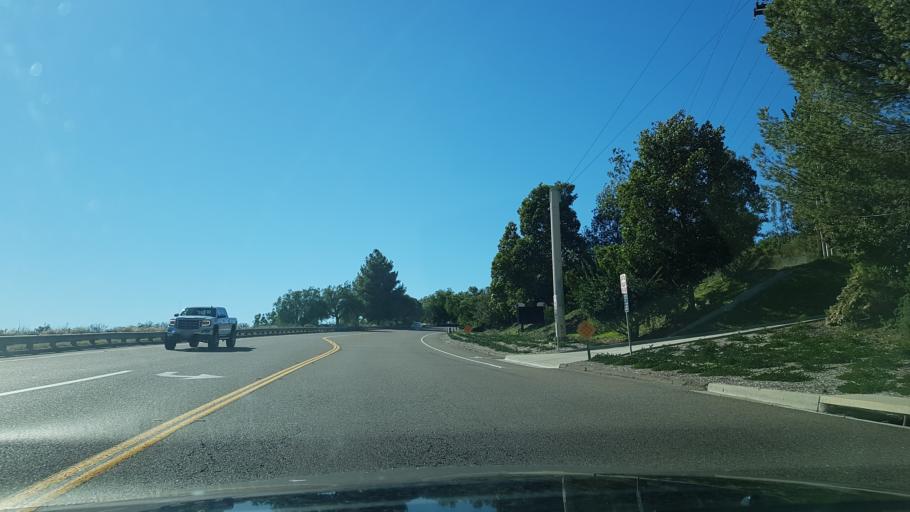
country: US
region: California
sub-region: San Diego County
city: Rancho Santa Fe
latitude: 33.0399
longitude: -117.1590
